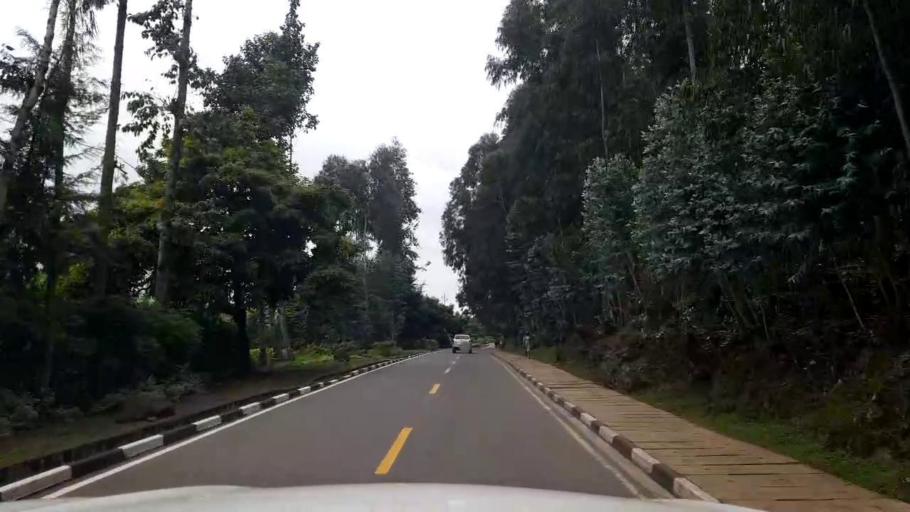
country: RW
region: Northern Province
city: Musanze
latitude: -1.4512
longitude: 29.5949
